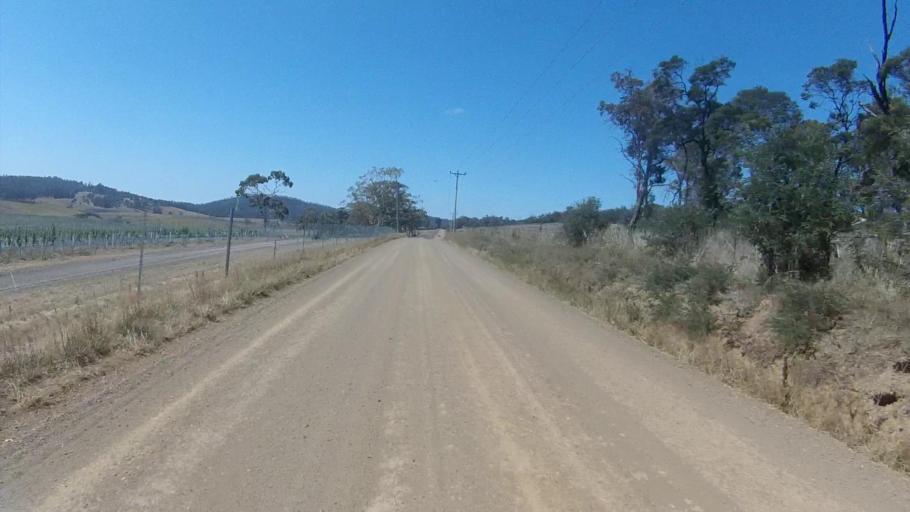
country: AU
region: Tasmania
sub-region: Sorell
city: Sorell
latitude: -42.8183
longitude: 147.6296
